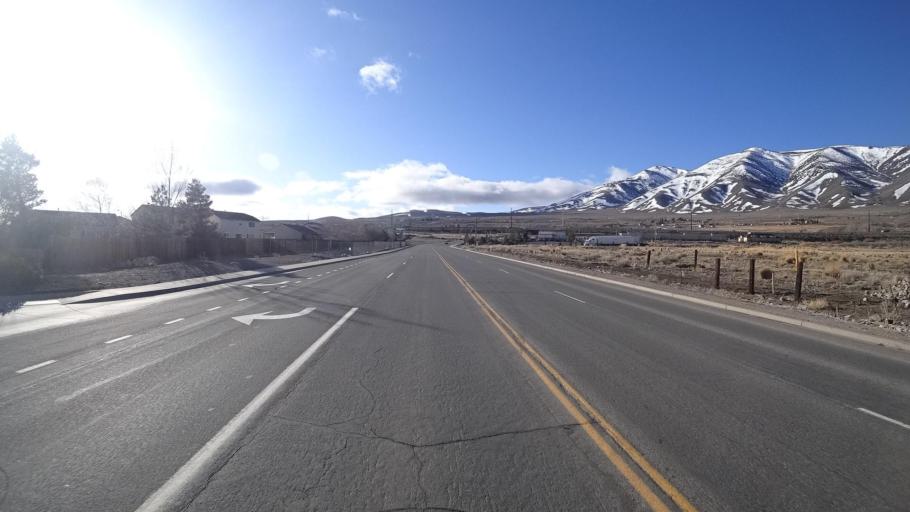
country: US
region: Nevada
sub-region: Washoe County
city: Lemmon Valley
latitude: 39.6304
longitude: -119.9164
